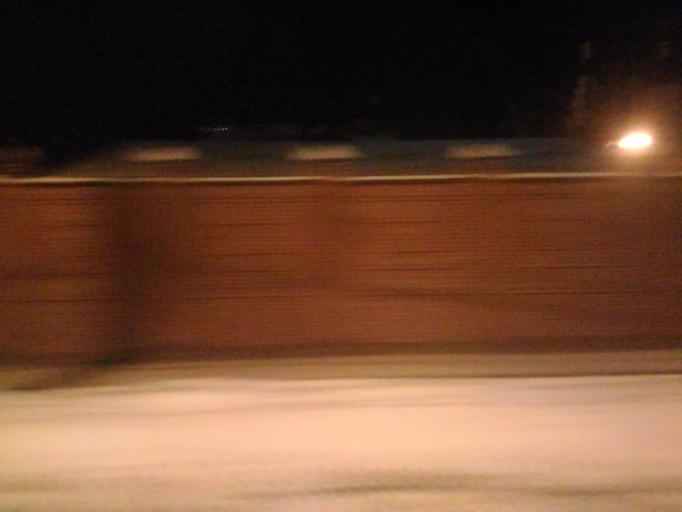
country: RU
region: Ulyanovsk
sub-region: Ulyanovskiy Rayon
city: Ulyanovsk
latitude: 54.3291
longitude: 48.4020
